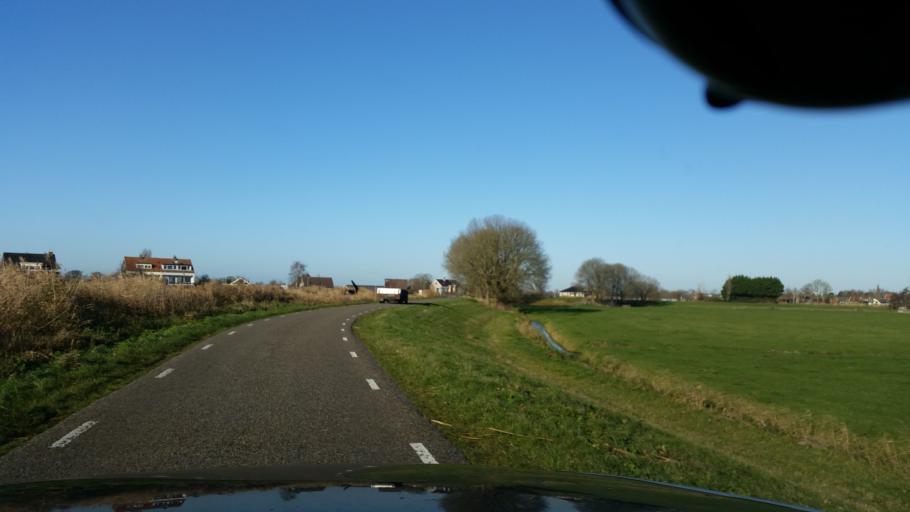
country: NL
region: Utrecht
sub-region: Gemeente De Ronde Venen
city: Mijdrecht
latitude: 52.2513
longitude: 4.8725
